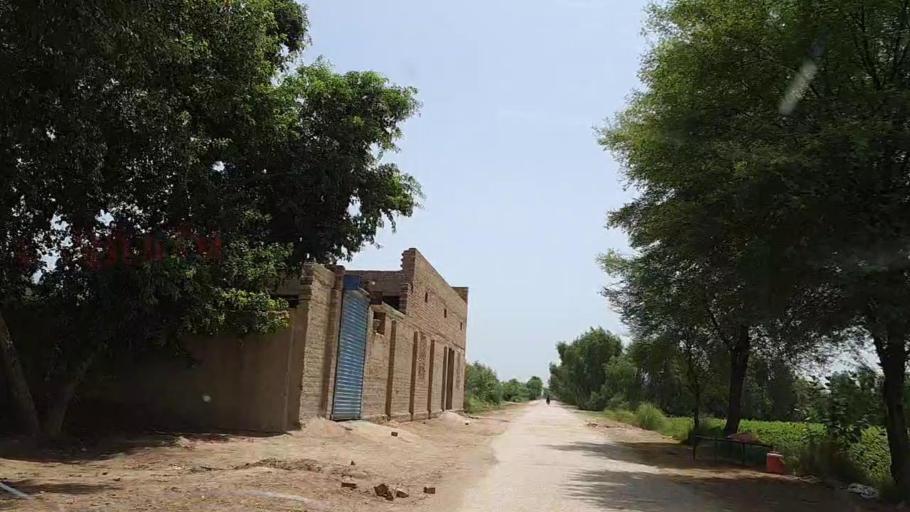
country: PK
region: Sindh
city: Tharu Shah
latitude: 26.9668
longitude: 68.0455
